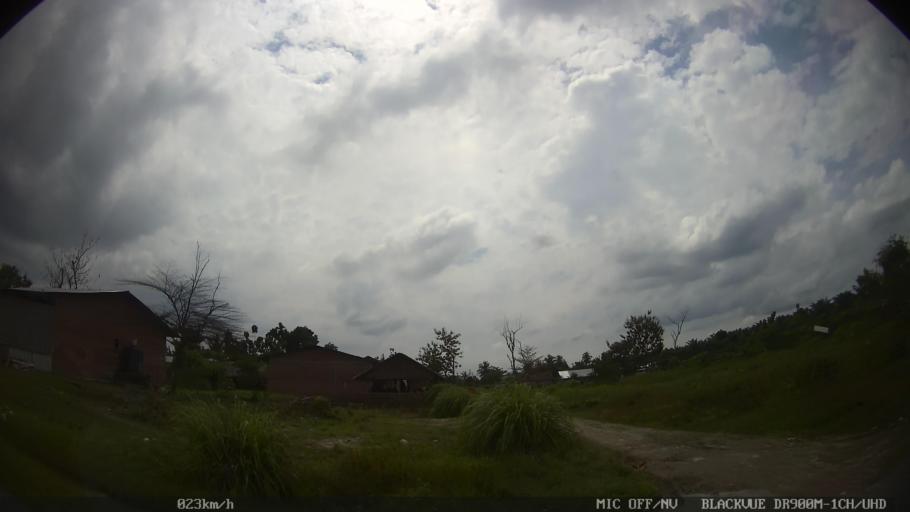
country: ID
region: North Sumatra
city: Sunggal
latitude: 3.6354
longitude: 98.6060
